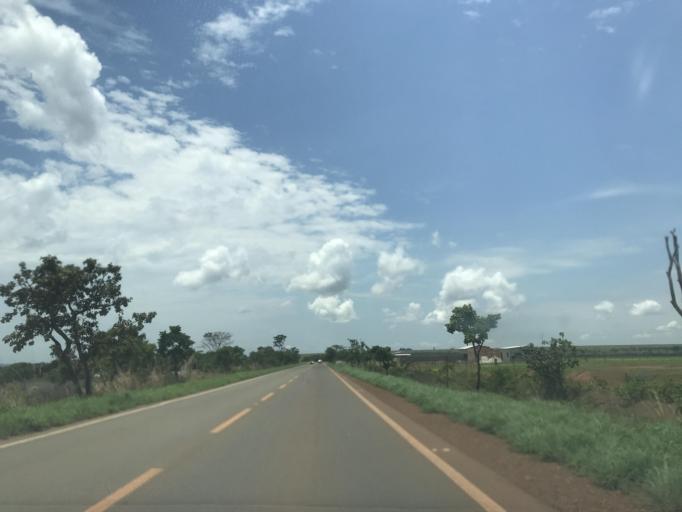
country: BR
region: Goias
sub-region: Luziania
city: Luziania
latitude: -16.4722
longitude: -48.2121
